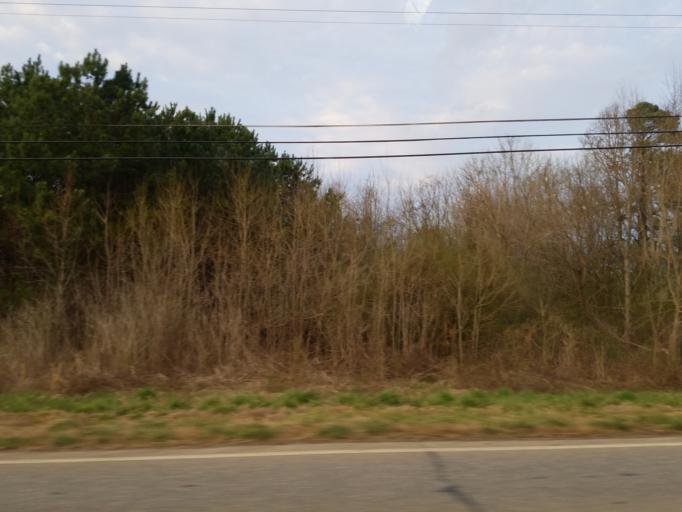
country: US
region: Georgia
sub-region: Pickens County
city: Jasper
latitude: 34.4650
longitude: -84.4647
